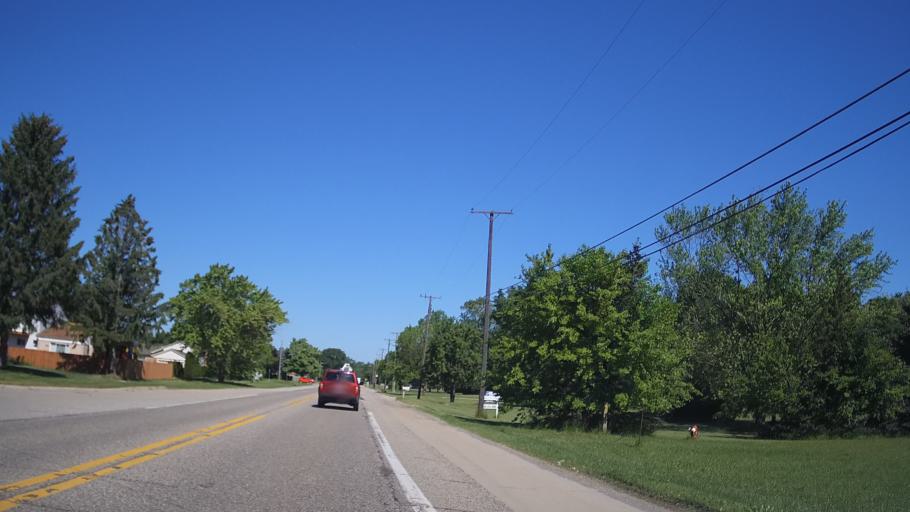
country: US
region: Michigan
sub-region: Macomb County
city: Sterling Heights
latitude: 42.5845
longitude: -82.9994
